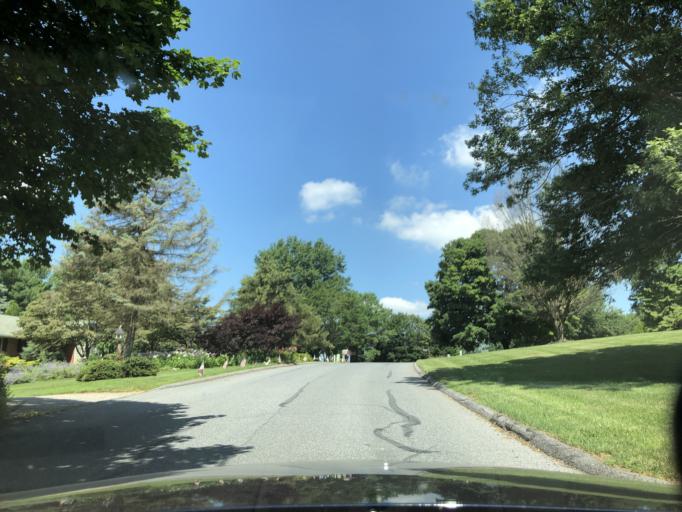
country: US
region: Maryland
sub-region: Carroll County
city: Westminster
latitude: 39.6198
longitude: -77.0011
